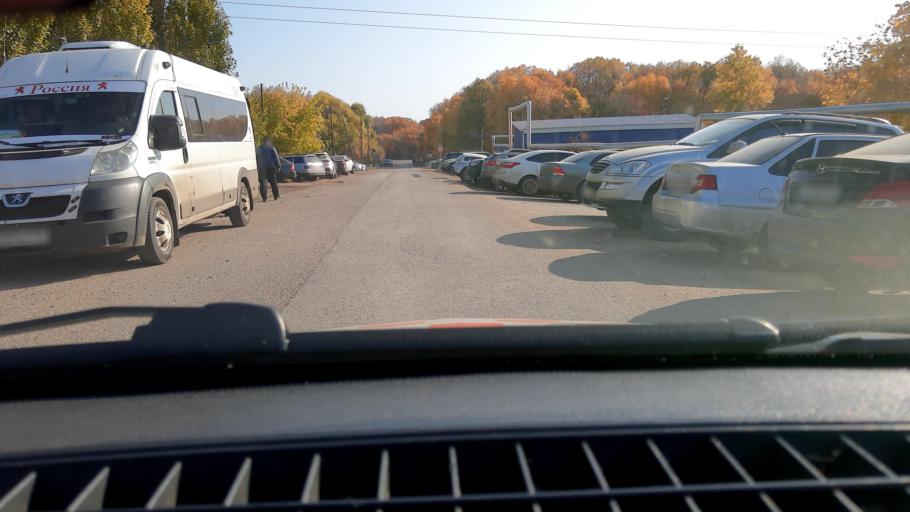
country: RU
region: Bashkortostan
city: Blagoveshchensk
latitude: 54.9457
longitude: 56.0736
